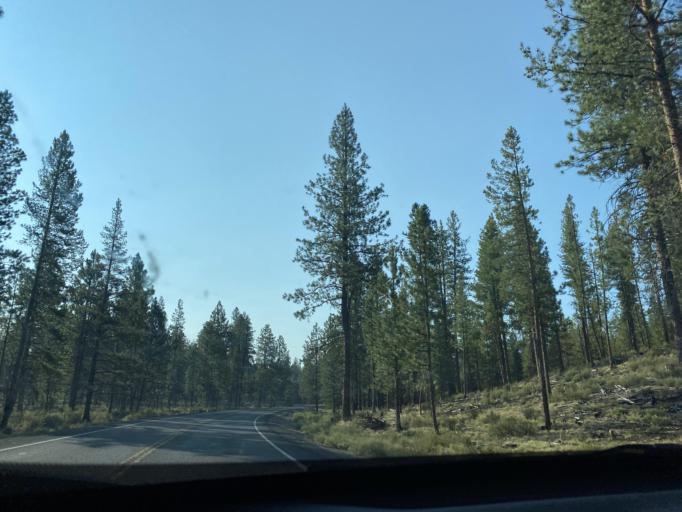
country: US
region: Oregon
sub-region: Deschutes County
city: La Pine
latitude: 43.7102
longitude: -121.4083
